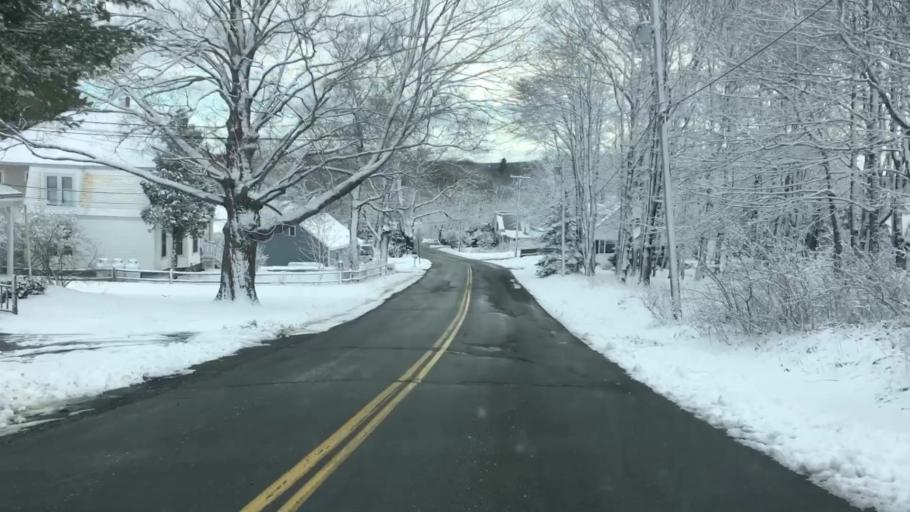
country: US
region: Maine
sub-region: Knox County
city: Rockland
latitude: 44.1105
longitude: -69.1261
